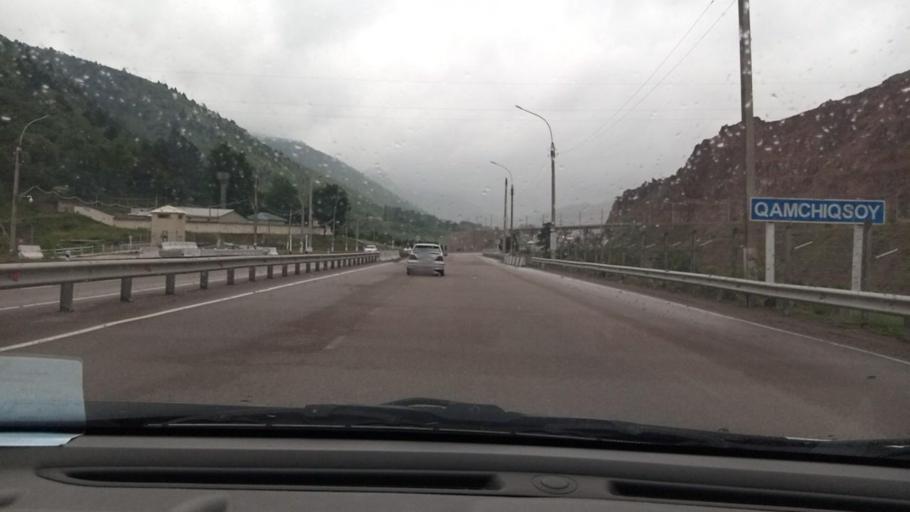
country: UZ
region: Toshkent
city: Angren
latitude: 41.1534
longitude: 70.4421
